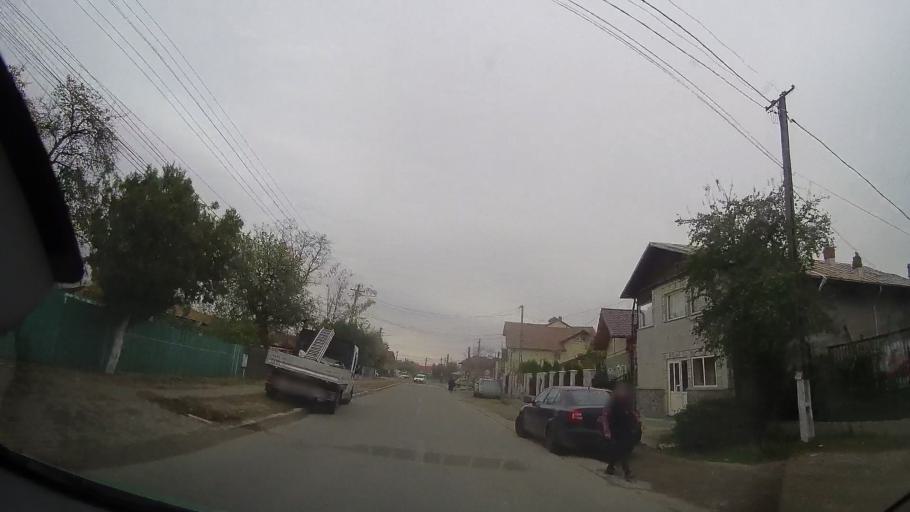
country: RO
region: Prahova
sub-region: Comuna Ceptura
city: Ceptura de Jos
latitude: 45.0144
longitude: 26.3323
